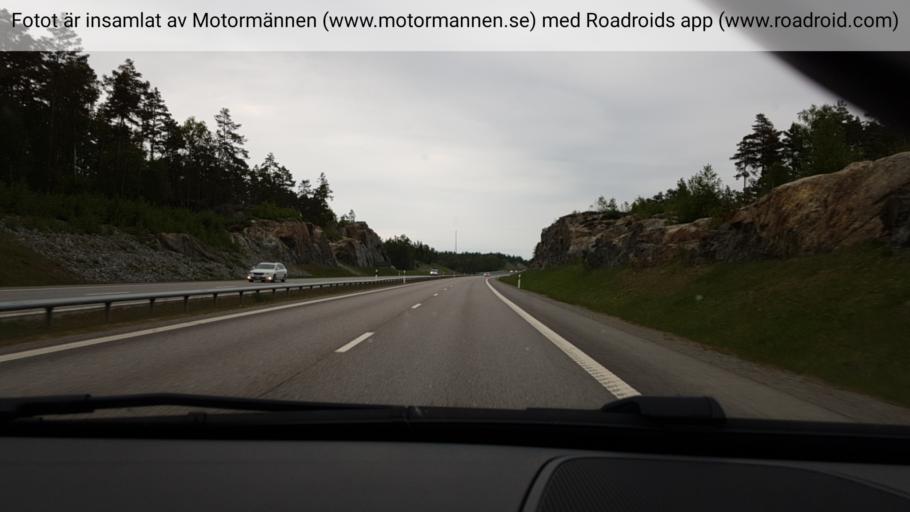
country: SE
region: Stockholm
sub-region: Nynashamns Kommun
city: Osmo
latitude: 59.0348
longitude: 17.9605
